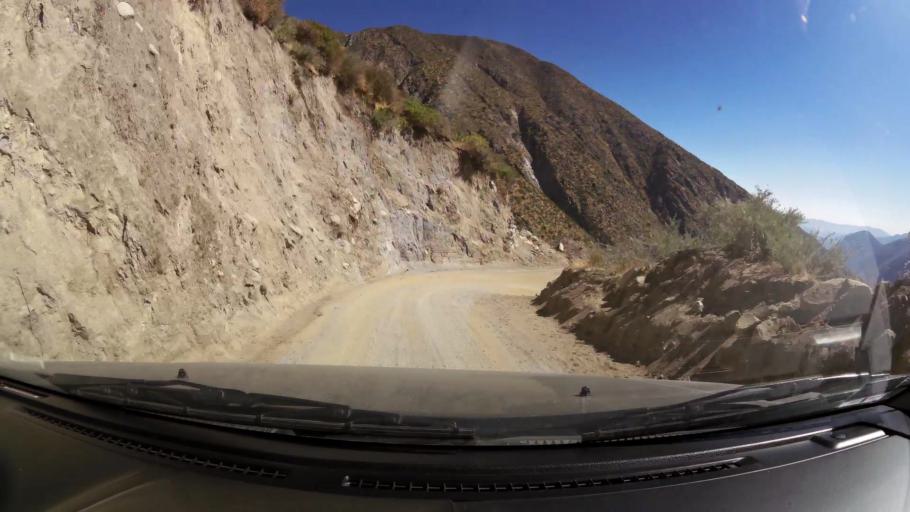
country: PE
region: Huancavelica
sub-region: Huaytara
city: Quito-Arma
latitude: -13.6180
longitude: -75.3544
